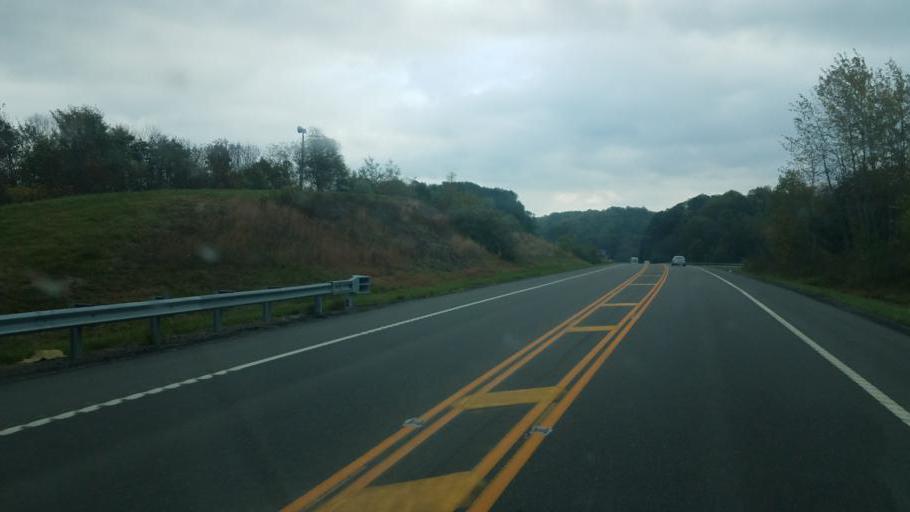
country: US
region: Ohio
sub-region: Tuscarawas County
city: Sugarcreek
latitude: 40.5070
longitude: -81.5816
